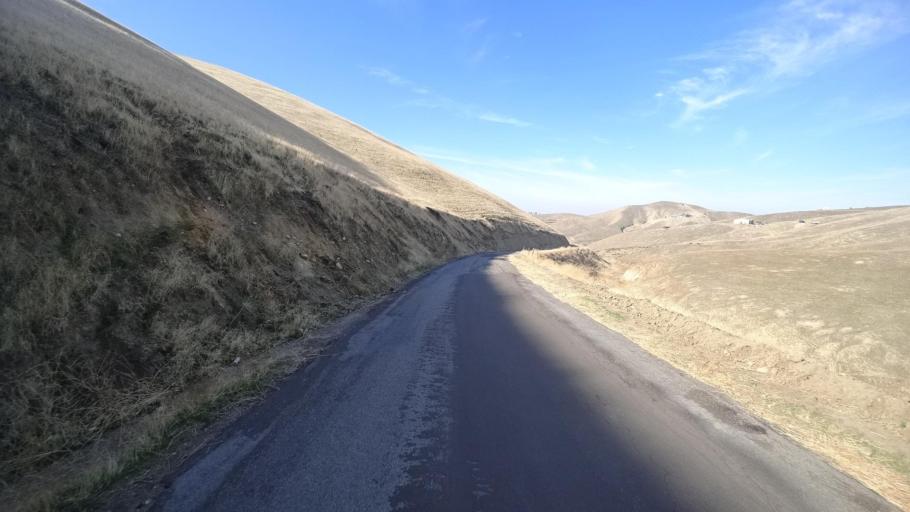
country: US
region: California
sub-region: Kern County
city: Lamont
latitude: 35.4023
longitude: -118.7878
